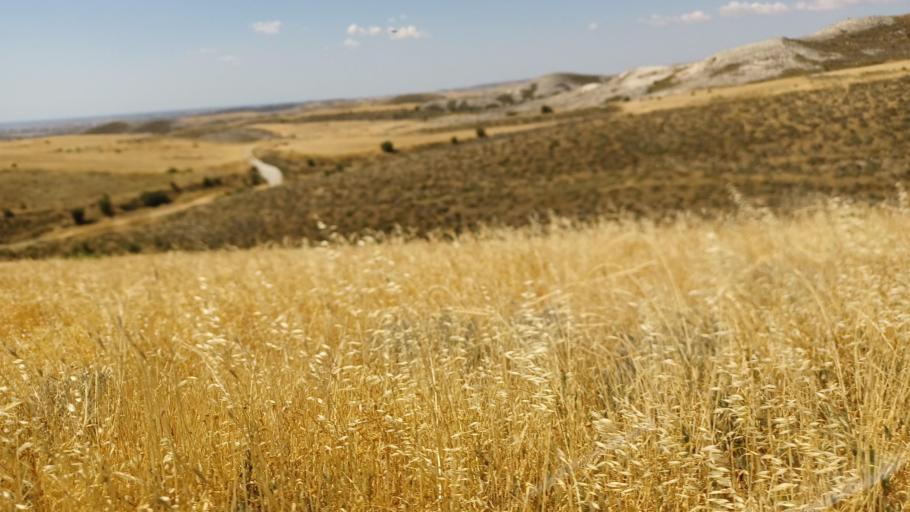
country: CY
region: Larnaka
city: Aradippou
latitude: 34.9936
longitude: 33.5666
